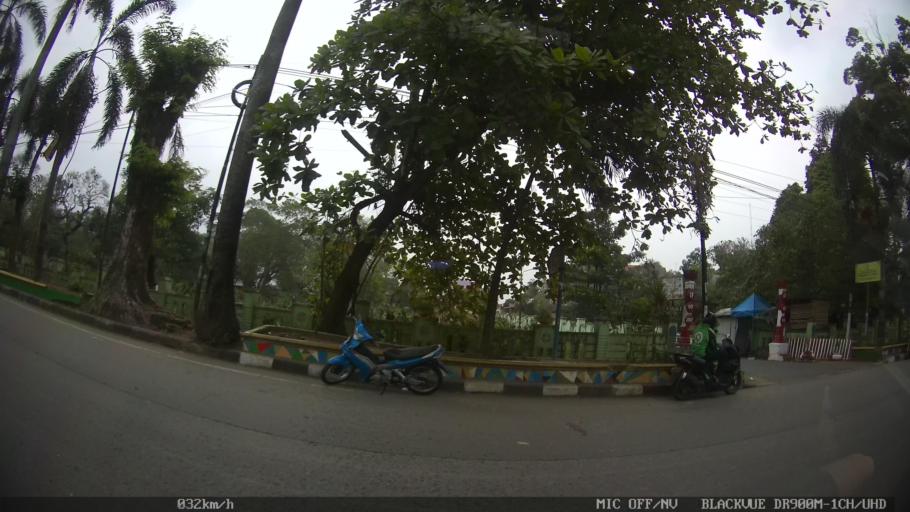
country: ID
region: North Sumatra
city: Deli Tua
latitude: 3.5426
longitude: 98.6986
